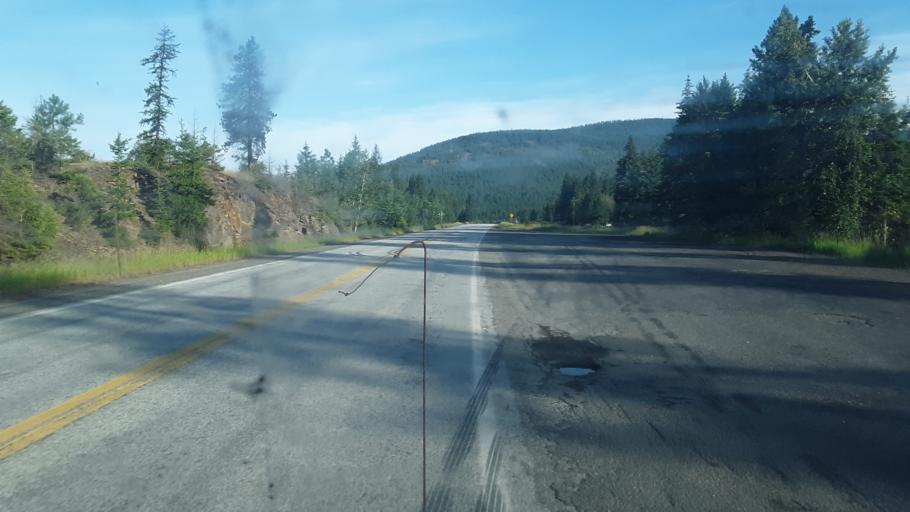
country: US
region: Idaho
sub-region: Boundary County
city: Bonners Ferry
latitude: 48.7232
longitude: -116.1701
